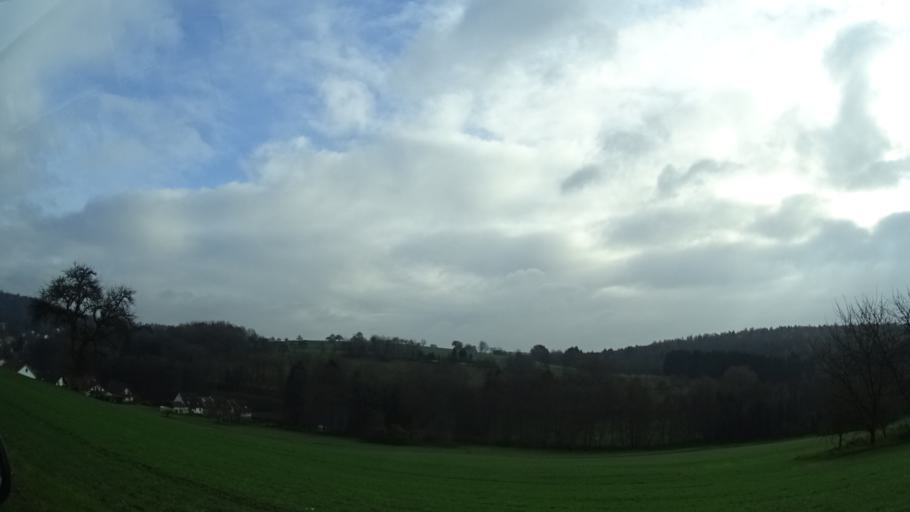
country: DE
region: Baden-Wuerttemberg
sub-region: Karlsruhe Region
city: Spechbach
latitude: 49.3731
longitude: 8.8812
